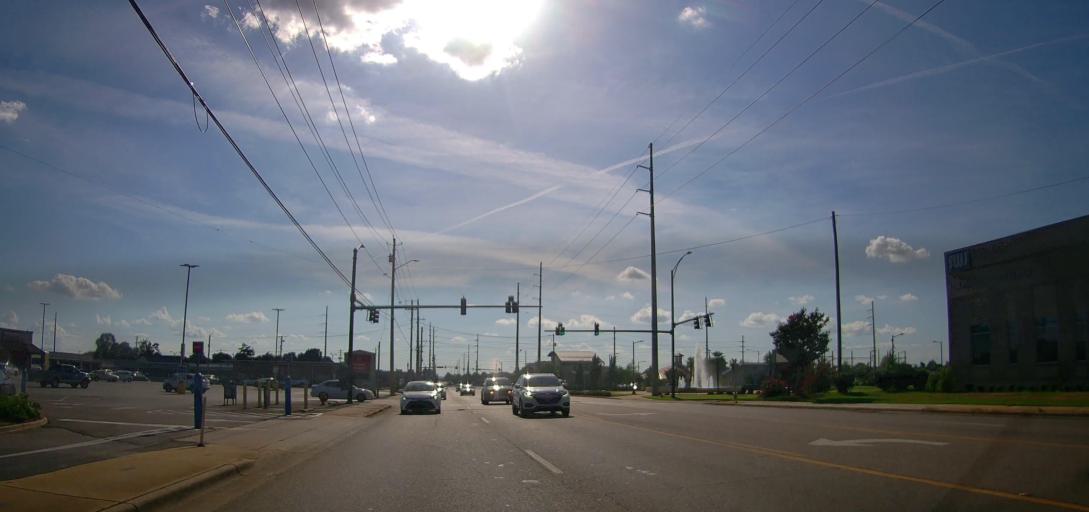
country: US
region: Alabama
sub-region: Tuscaloosa County
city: Holt
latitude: 33.2064
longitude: -87.5015
